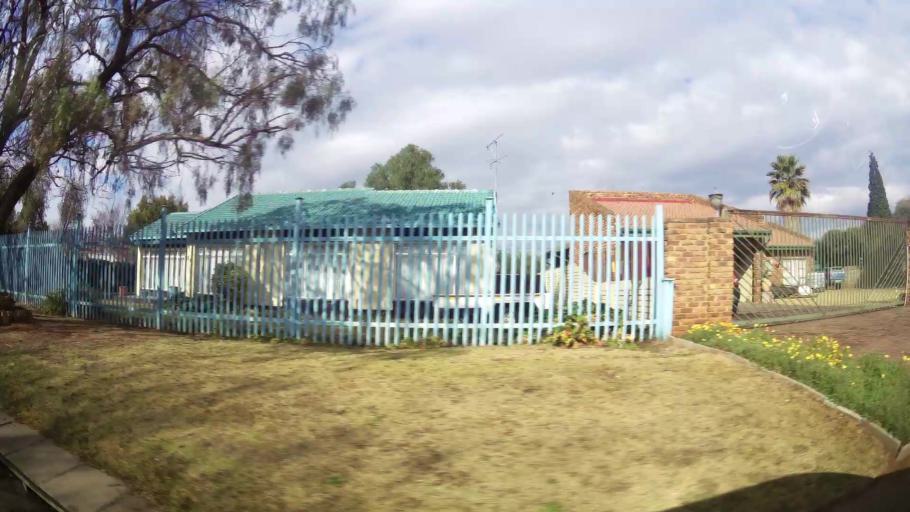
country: ZA
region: Gauteng
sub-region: Sedibeng District Municipality
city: Meyerton
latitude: -26.5528
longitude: 28.0349
